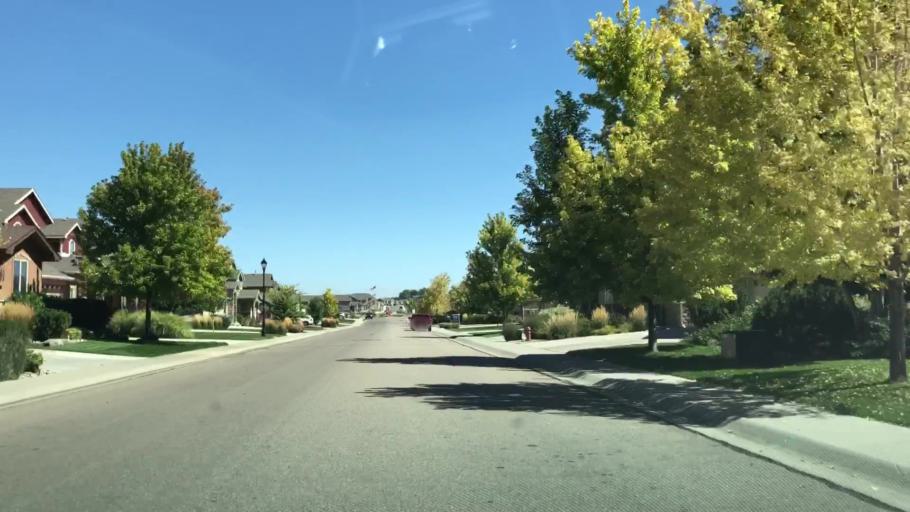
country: US
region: Colorado
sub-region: Weld County
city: Johnstown
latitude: 40.3993
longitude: -104.9769
